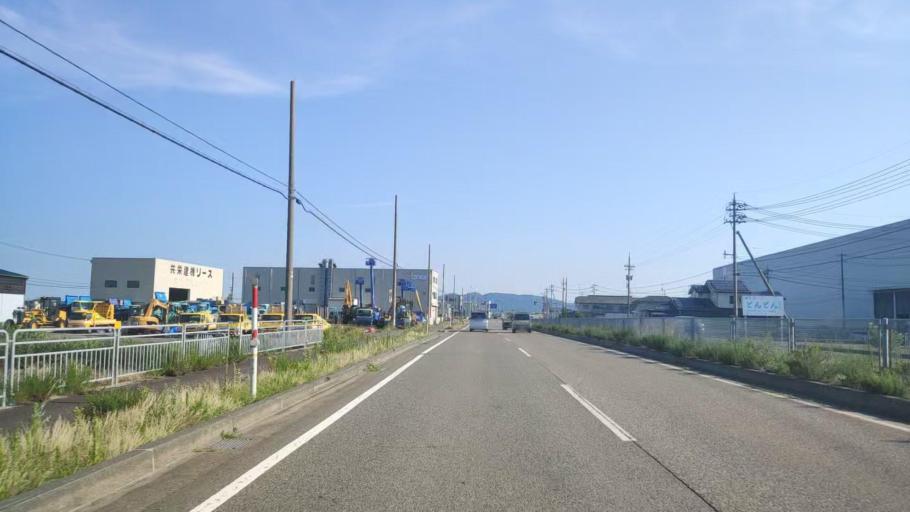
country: JP
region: Fukui
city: Maruoka
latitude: 36.1649
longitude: 136.2635
